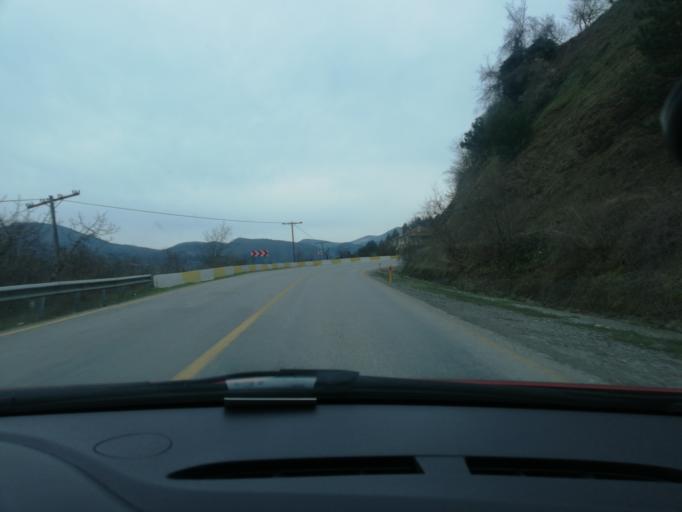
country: TR
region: Kastamonu
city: Inebolu
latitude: 41.9452
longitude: 33.7622
